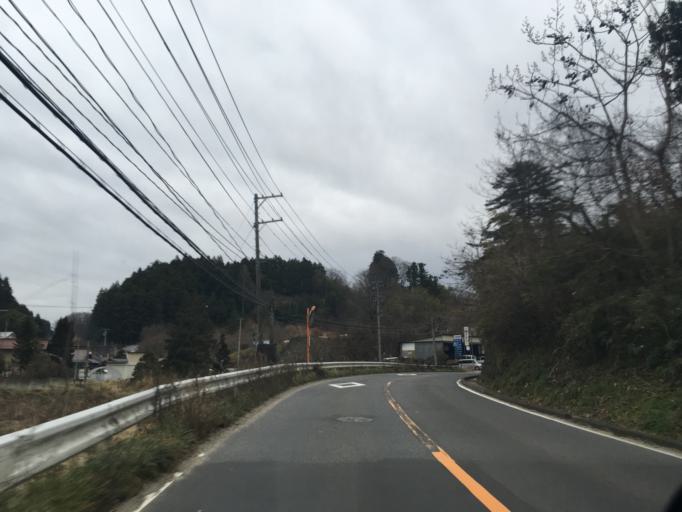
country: JP
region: Fukushima
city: Koriyama
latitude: 37.3691
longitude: 140.4462
